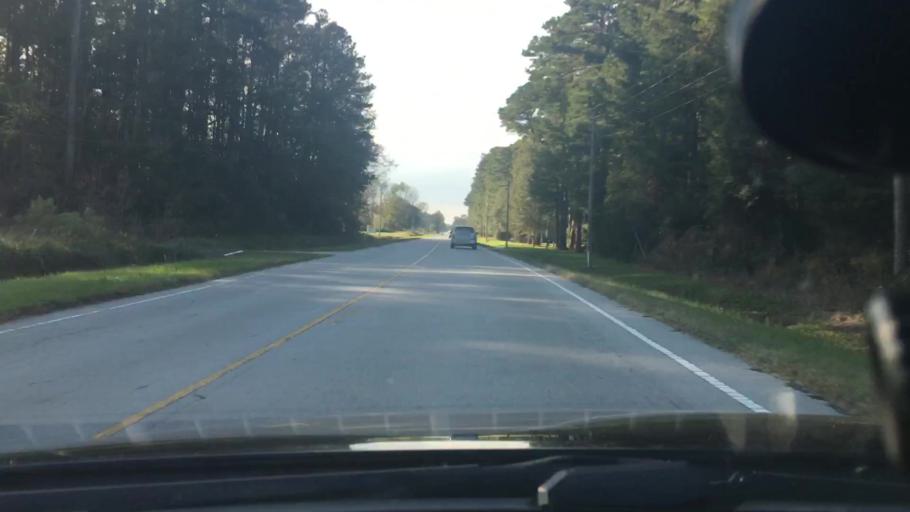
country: US
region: North Carolina
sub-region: Pitt County
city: Windsor
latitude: 35.4697
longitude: -77.2807
